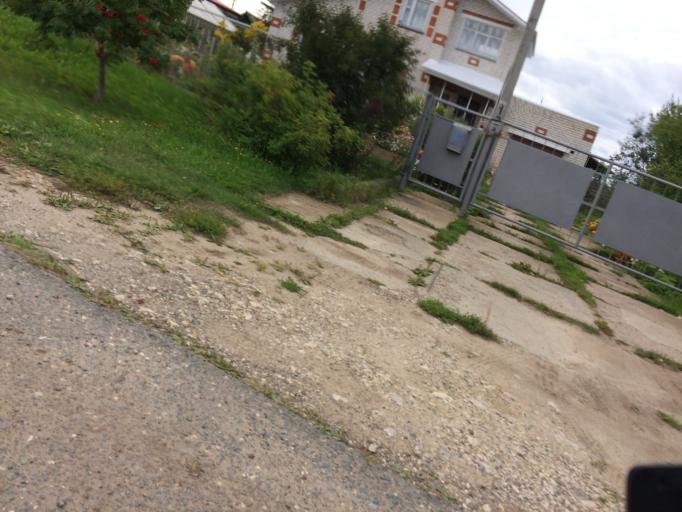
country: RU
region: Mariy-El
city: Yoshkar-Ola
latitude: 56.6659
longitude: 48.0009
